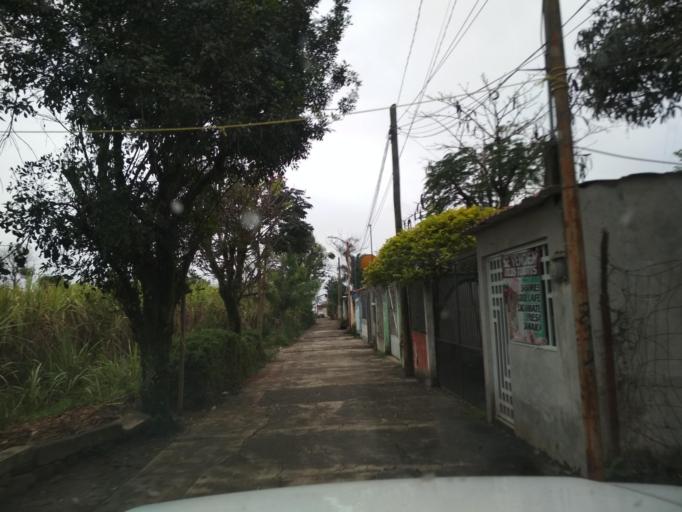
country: MX
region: Veracruz
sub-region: Cordoba
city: Veinte de Noviembre
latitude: 18.8683
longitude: -96.9554
